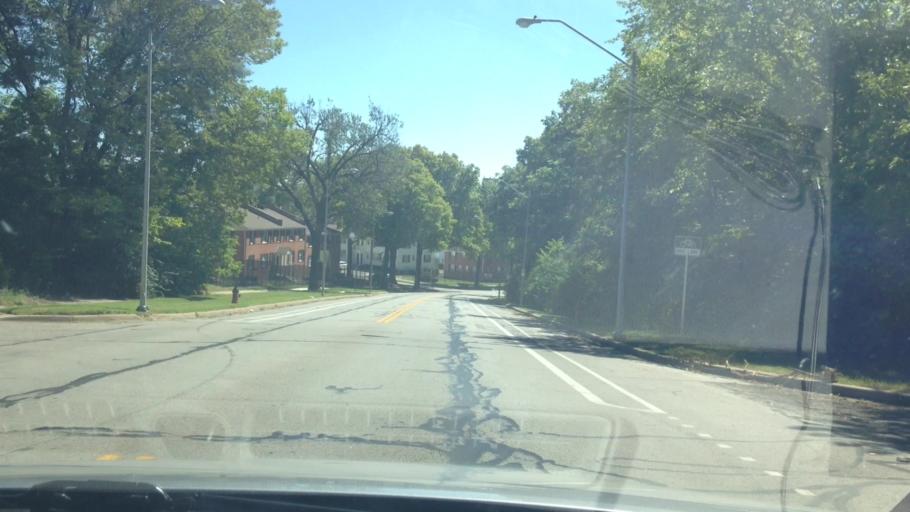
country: US
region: Missouri
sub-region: Jackson County
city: Kansas City
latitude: 39.0407
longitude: -94.5433
